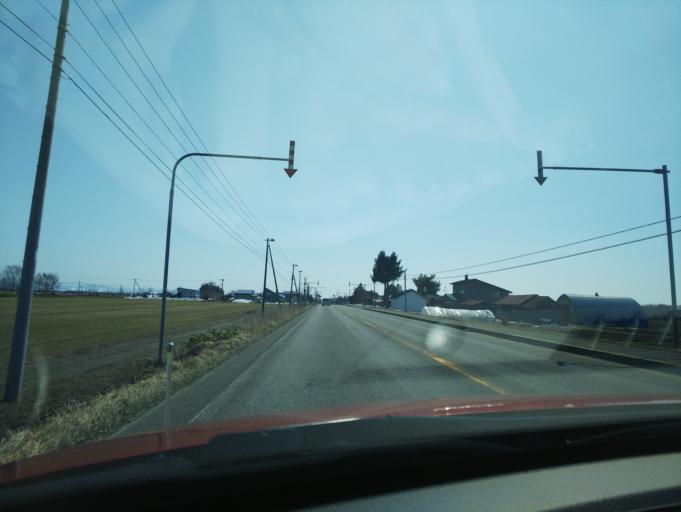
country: JP
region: Hokkaido
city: Nayoro
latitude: 44.2483
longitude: 142.3947
